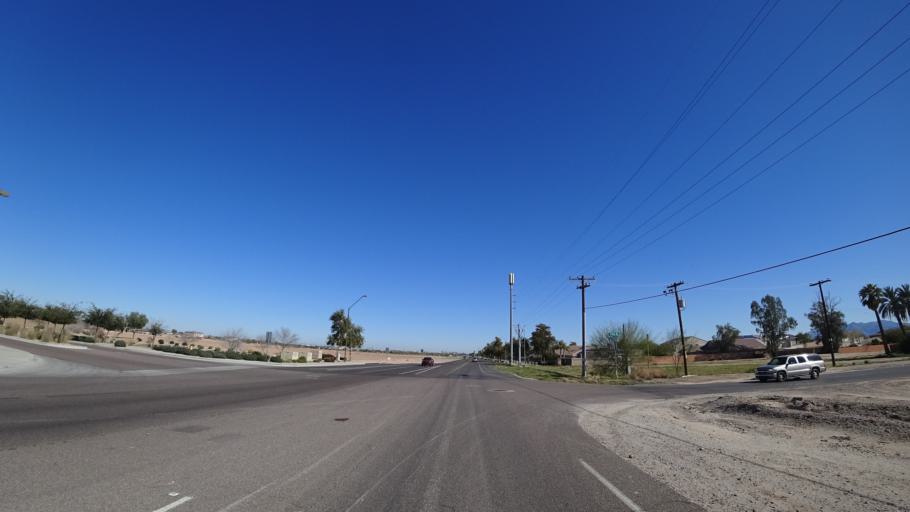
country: US
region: Arizona
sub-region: Maricopa County
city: Goodyear
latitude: 33.4357
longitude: -112.4366
